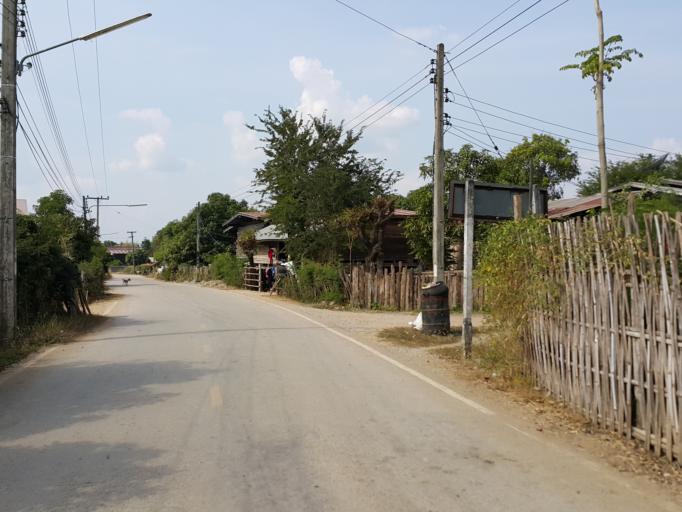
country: TH
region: Sukhothai
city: Thung Saliam
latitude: 17.3242
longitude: 99.4479
